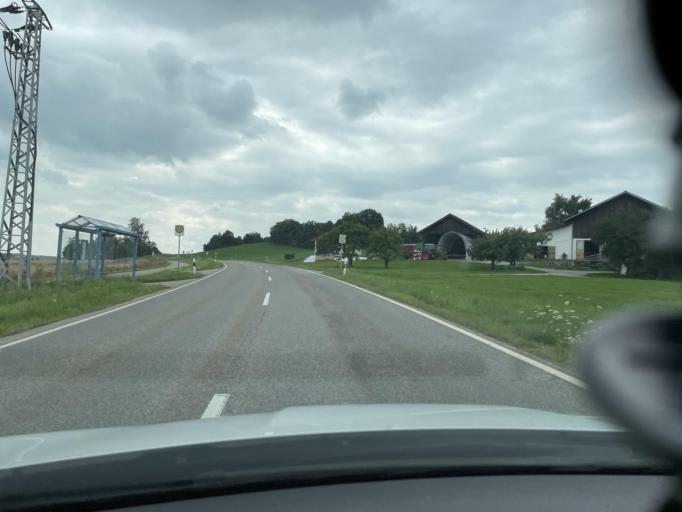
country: DE
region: Bavaria
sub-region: Upper Bavaria
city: Haag in Oberbayern
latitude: 48.1797
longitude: 12.1574
